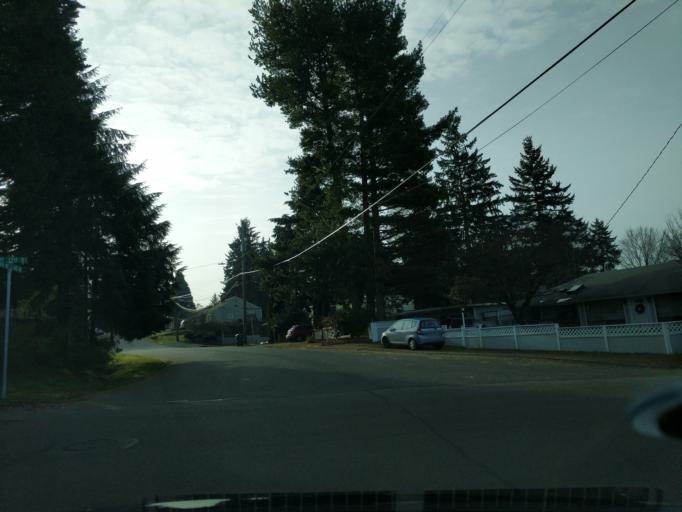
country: US
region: Washington
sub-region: King County
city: Shoreline
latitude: 47.7524
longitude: -122.3281
